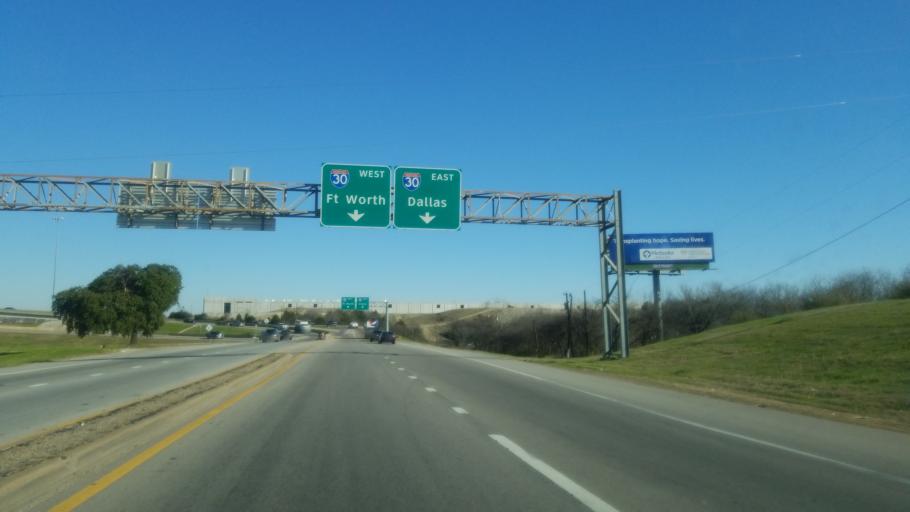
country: US
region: Texas
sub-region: Dallas County
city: Cockrell Hill
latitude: 32.7644
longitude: -96.9125
